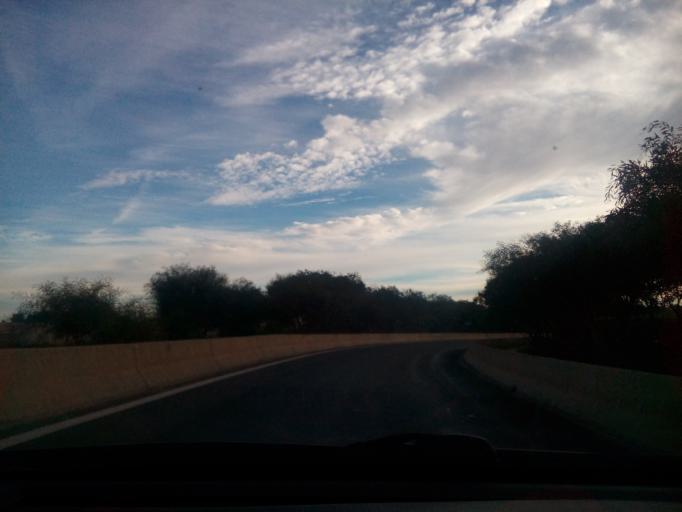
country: DZ
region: Relizane
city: Relizane
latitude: 35.7364
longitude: 0.3077
